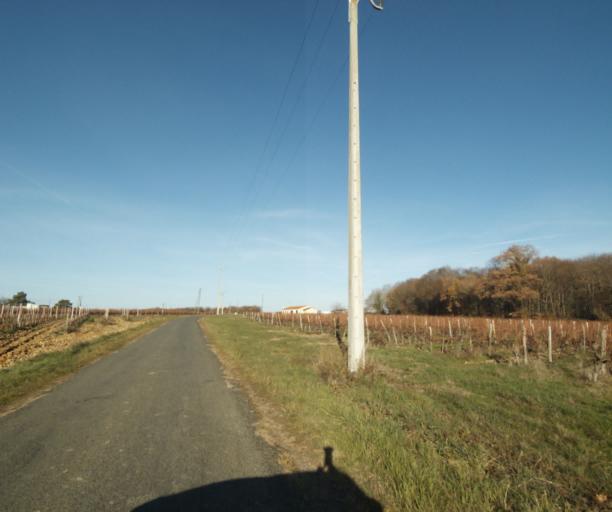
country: FR
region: Poitou-Charentes
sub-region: Departement de la Charente-Maritime
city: Cherac
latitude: 45.7272
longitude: -0.4460
